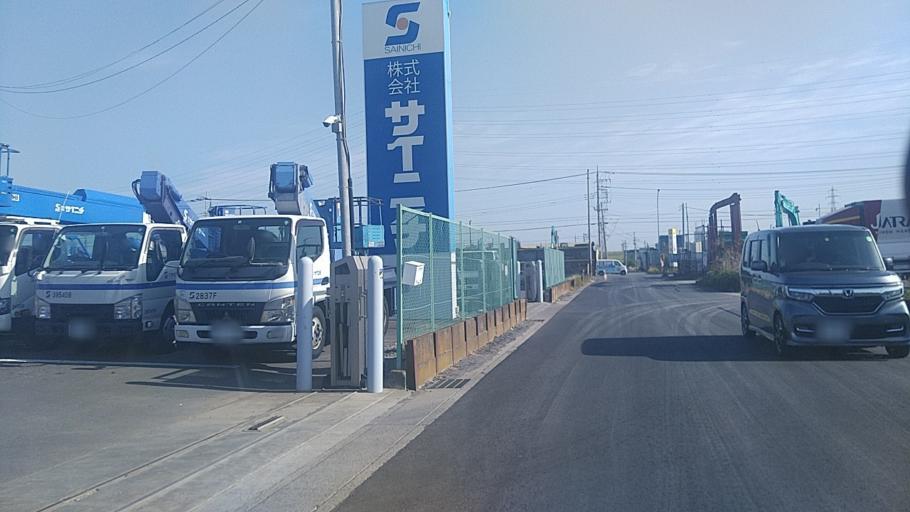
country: JP
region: Saitama
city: Wako
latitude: 35.7964
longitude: 139.6360
